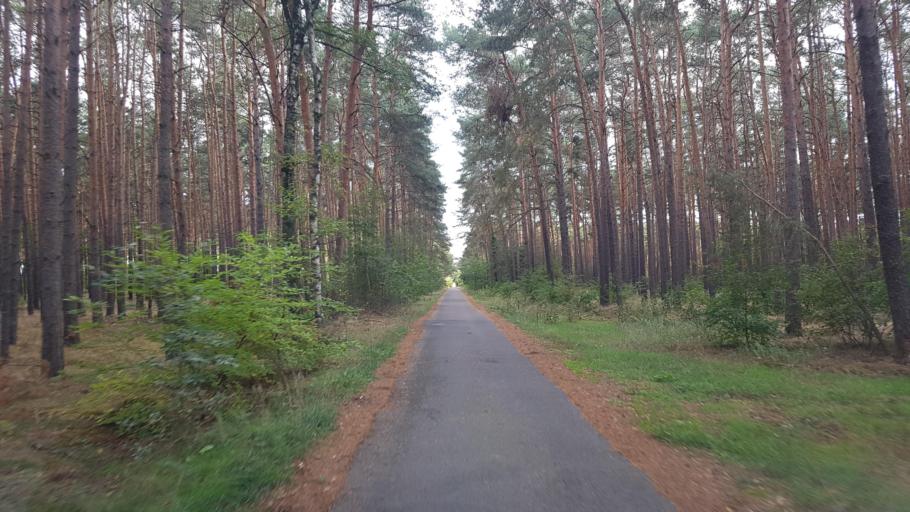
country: DE
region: Brandenburg
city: Ihlow
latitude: 51.8582
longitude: 13.2617
